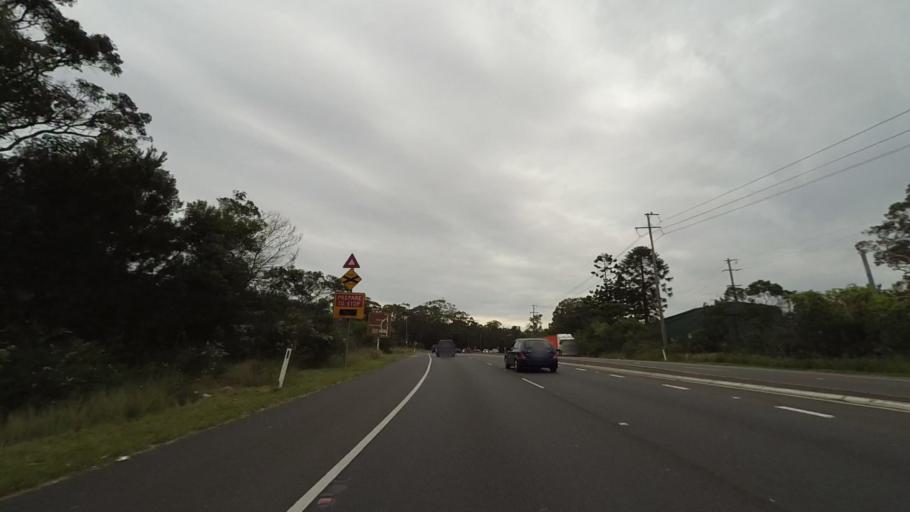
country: AU
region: New South Wales
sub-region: Sutherland Shire
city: Loftus
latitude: -34.0481
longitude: 151.0521
